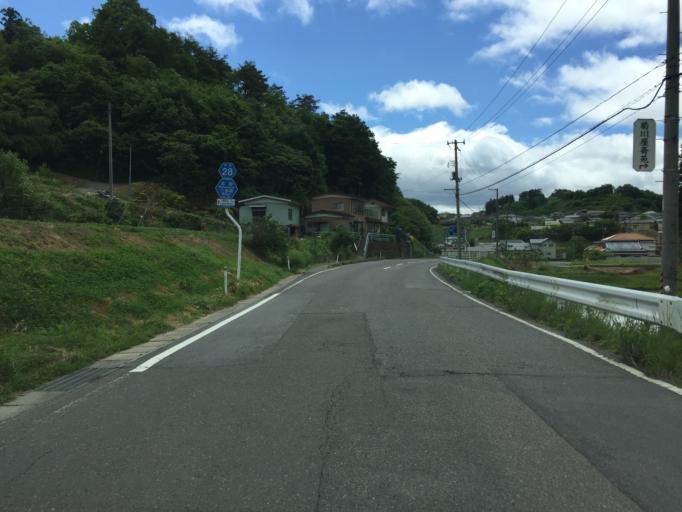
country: JP
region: Fukushima
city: Miharu
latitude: 37.4529
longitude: 140.4725
